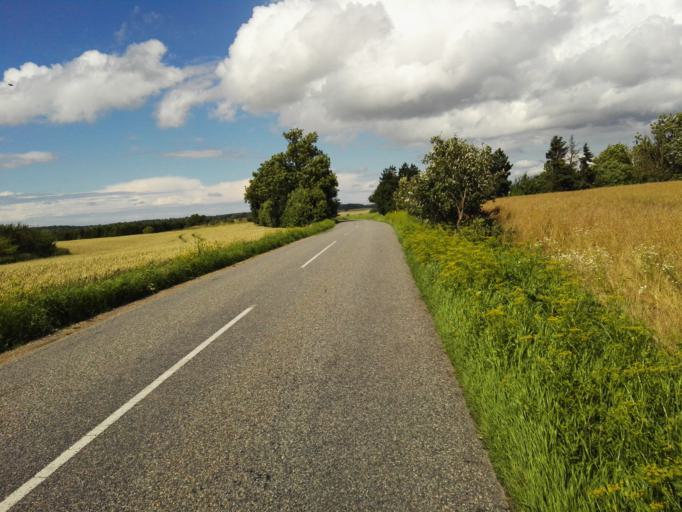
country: DK
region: Capital Region
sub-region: Egedal Kommune
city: Vekso
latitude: 55.7837
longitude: 12.2339
